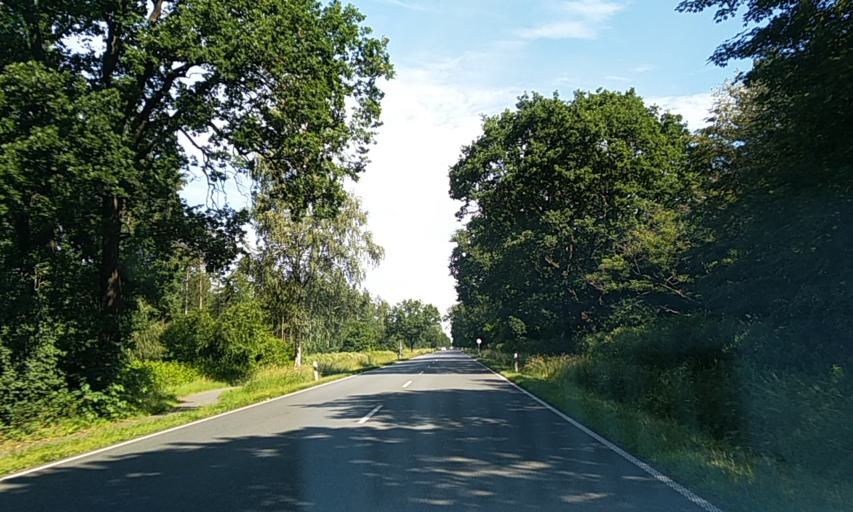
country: DE
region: Schleswig-Holstein
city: Lohe-Fohrden
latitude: 54.3784
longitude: 9.5456
